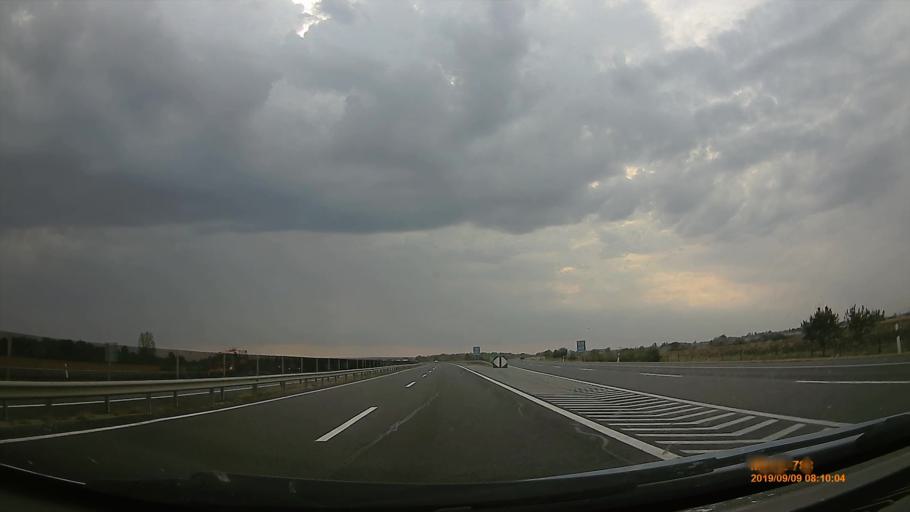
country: HU
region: Hajdu-Bihar
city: Gorbehaza
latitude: 47.7955
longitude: 21.2444
